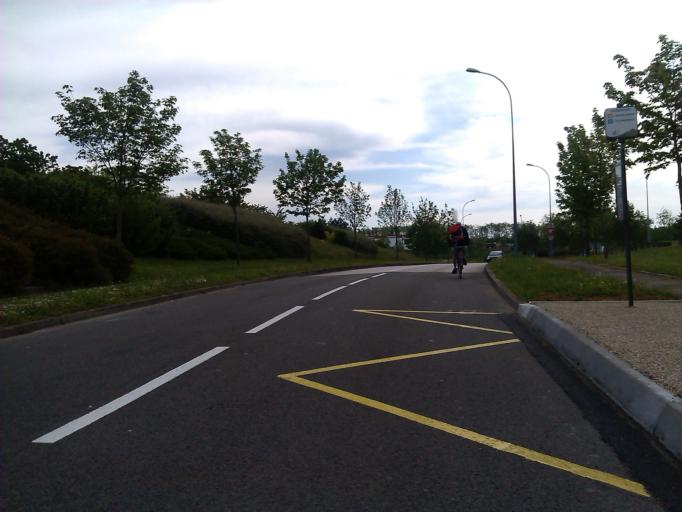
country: FR
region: Franche-Comte
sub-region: Departement du Jura
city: Dole
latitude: 47.1070
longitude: 5.5024
